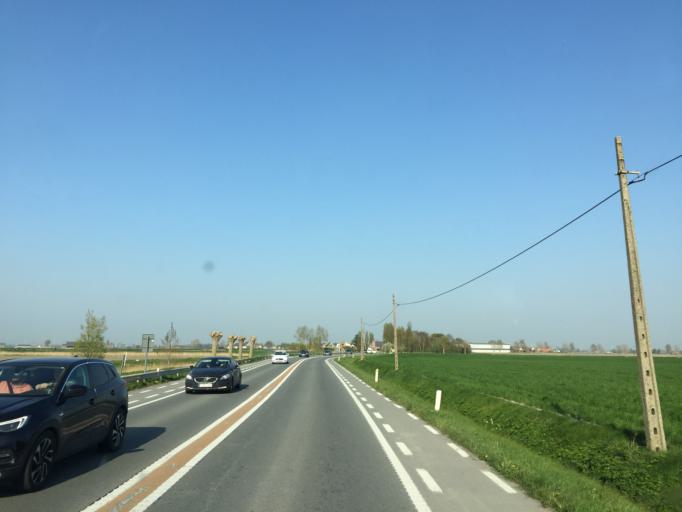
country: BE
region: Flanders
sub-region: Provincie West-Vlaanderen
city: Jabbeke
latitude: 51.2385
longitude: 3.1010
